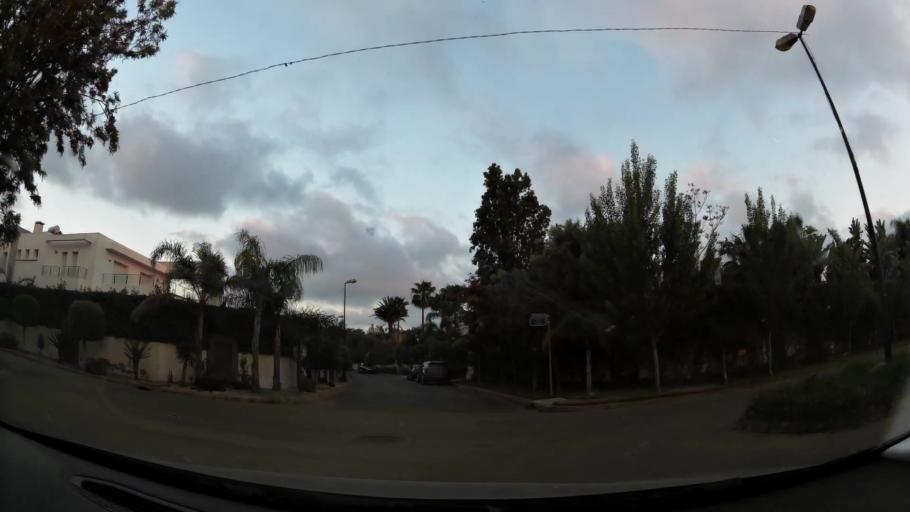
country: MA
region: Rabat-Sale-Zemmour-Zaer
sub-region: Rabat
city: Rabat
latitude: 33.9683
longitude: -6.8364
